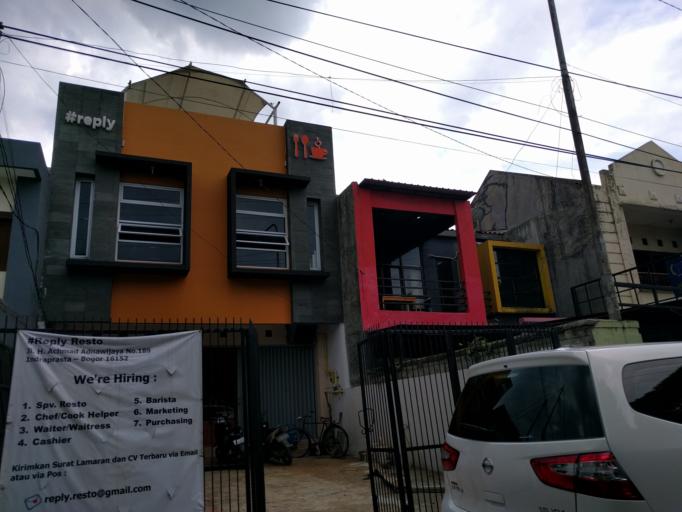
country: ID
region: West Java
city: Bogor
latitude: -6.5898
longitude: 106.8167
